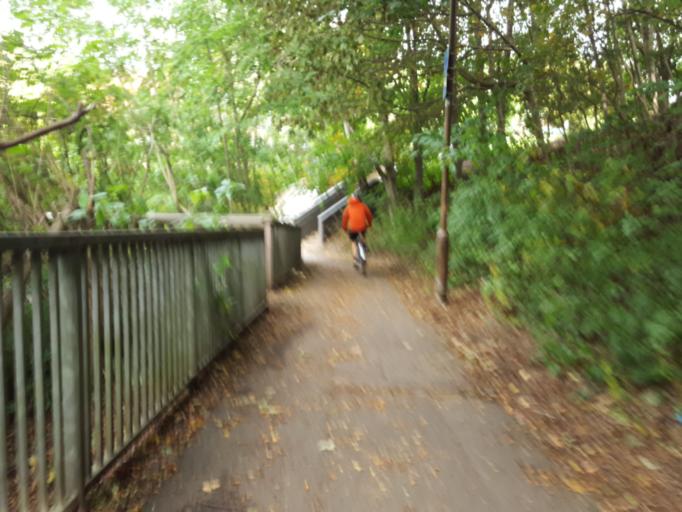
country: GB
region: Scotland
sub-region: West Lothian
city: Livingston
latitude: 55.8869
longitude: -3.5437
